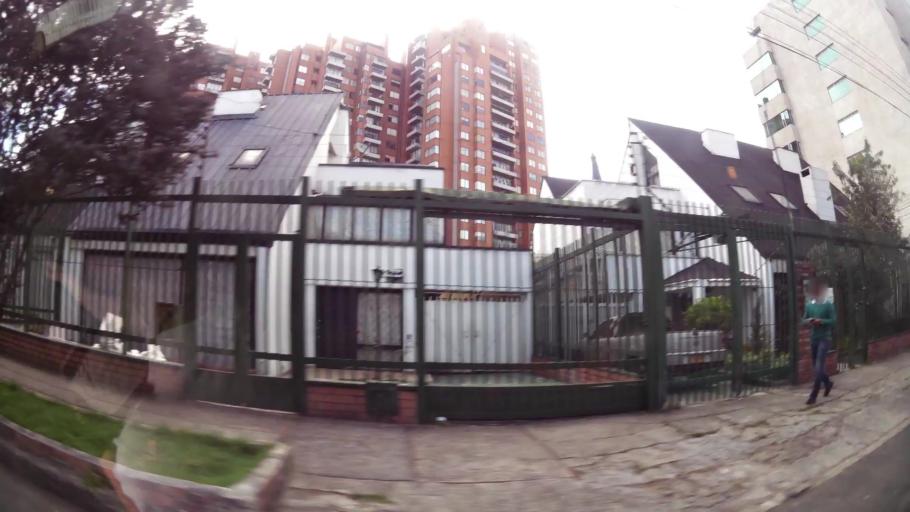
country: CO
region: Bogota D.C.
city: Barrio San Luis
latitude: 4.6905
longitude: -74.0708
